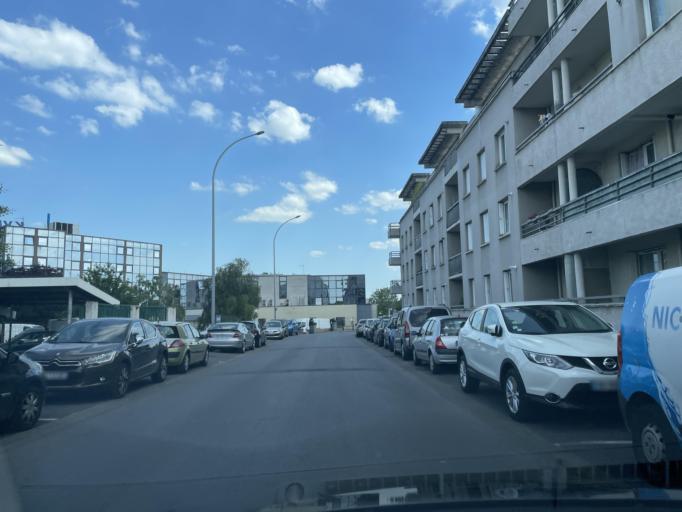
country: FR
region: Ile-de-France
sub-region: Departement du Val-de-Marne
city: Bonneuil-sur-Marne
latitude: 48.7688
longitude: 2.4857
